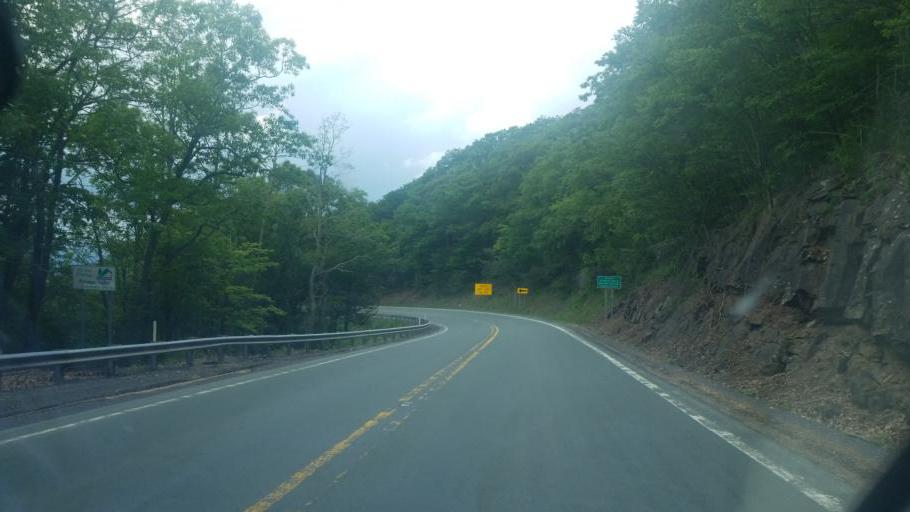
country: US
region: West Virginia
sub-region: Pendleton County
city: Franklin
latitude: 38.5818
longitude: -79.1667
